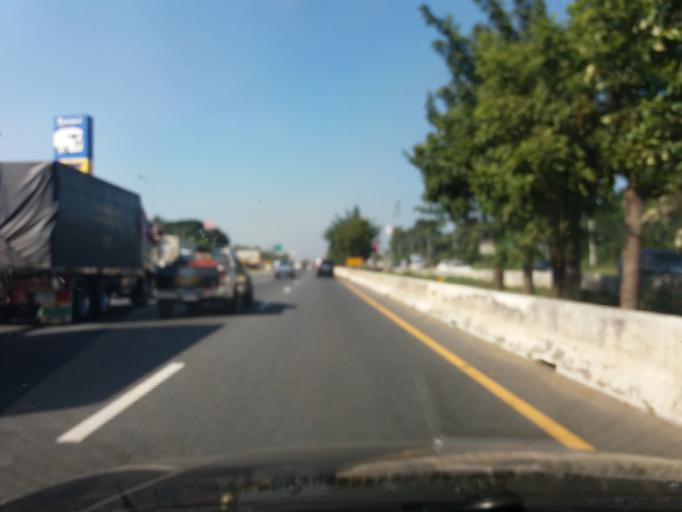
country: TH
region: Nakhon Sawan
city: Krok Phra
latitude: 15.5682
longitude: 100.1258
